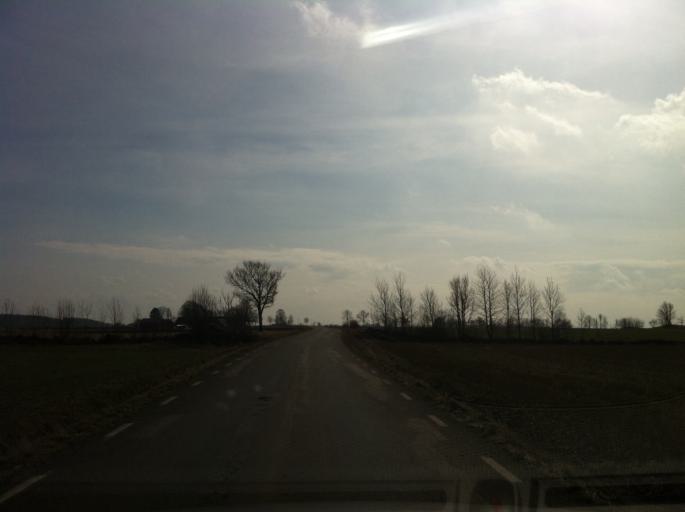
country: SE
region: Vaestra Goetaland
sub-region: Falkopings Kommun
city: Falkoeping
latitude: 58.2225
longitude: 13.4744
